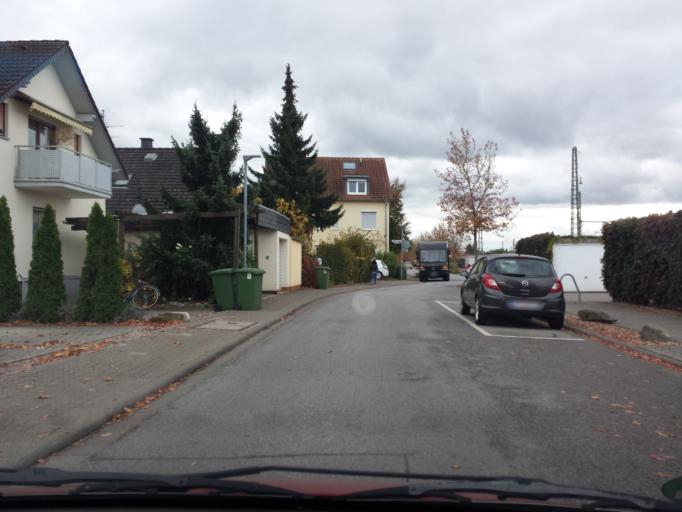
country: DE
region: Hesse
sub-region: Regierungsbezirk Darmstadt
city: Bensheim
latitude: 49.7013
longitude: 8.6139
